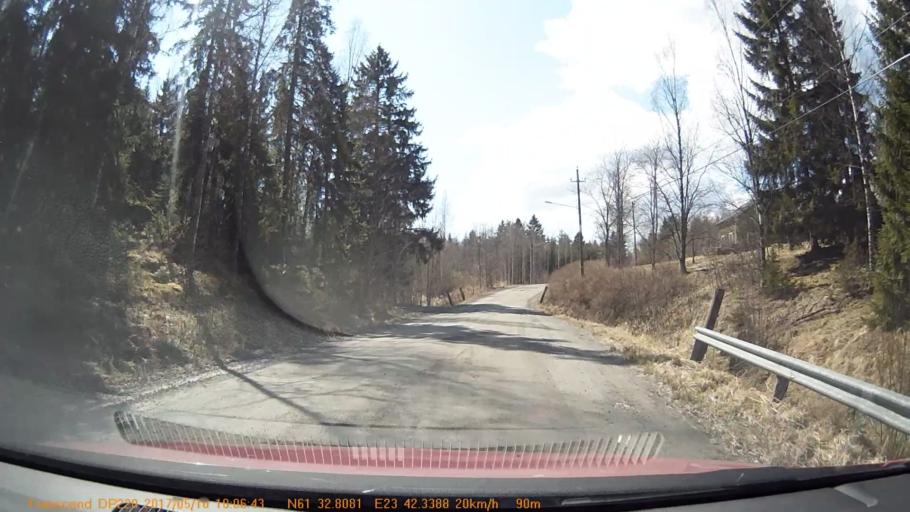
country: FI
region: Pirkanmaa
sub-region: Tampere
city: Tampere
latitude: 61.5469
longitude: 23.7057
